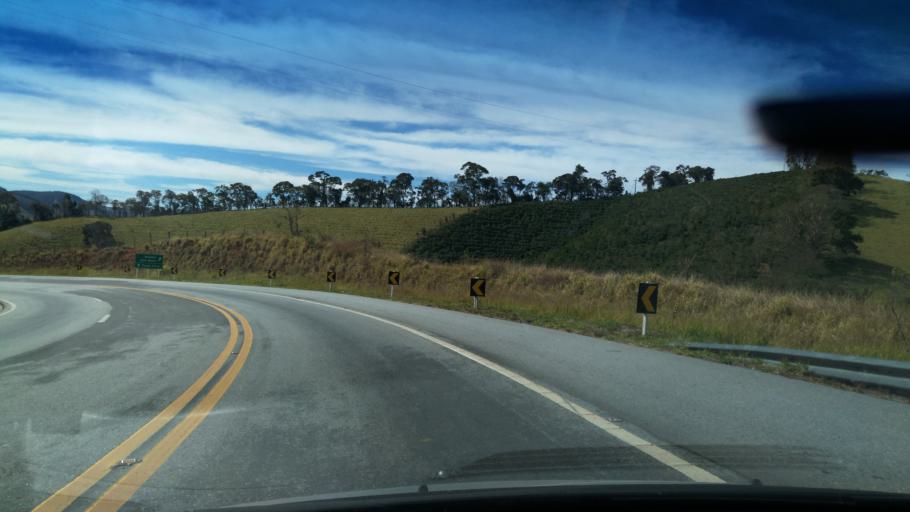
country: BR
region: Minas Gerais
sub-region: Borda Da Mata
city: Borda da Mata
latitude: -22.1357
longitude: -46.1571
